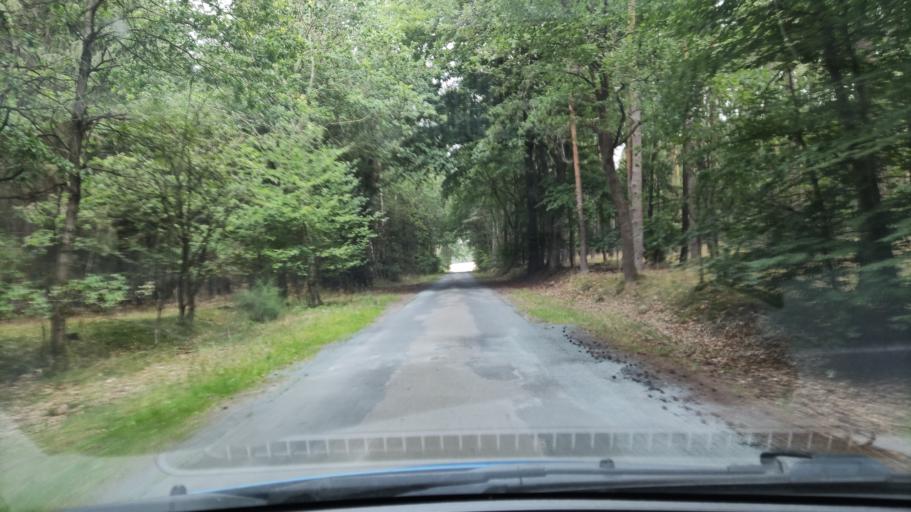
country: DE
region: Lower Saxony
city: Schnega
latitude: 52.9283
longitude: 10.8805
